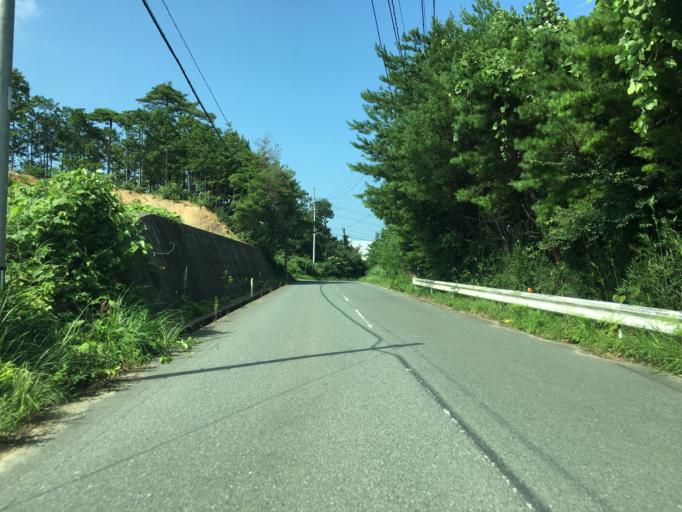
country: JP
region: Miyagi
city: Marumori
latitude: 37.8966
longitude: 140.8897
